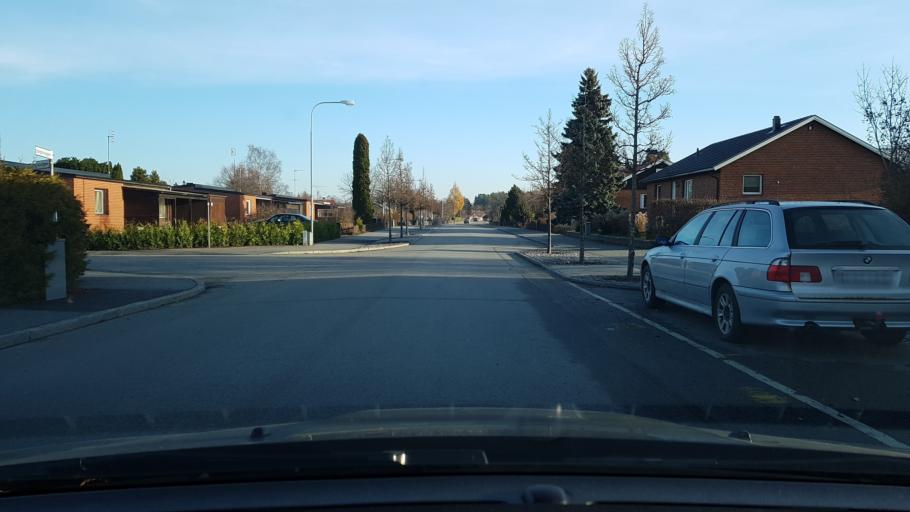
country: SE
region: Stockholm
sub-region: Norrtalje Kommun
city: Rimbo
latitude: 59.7405
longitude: 18.3496
